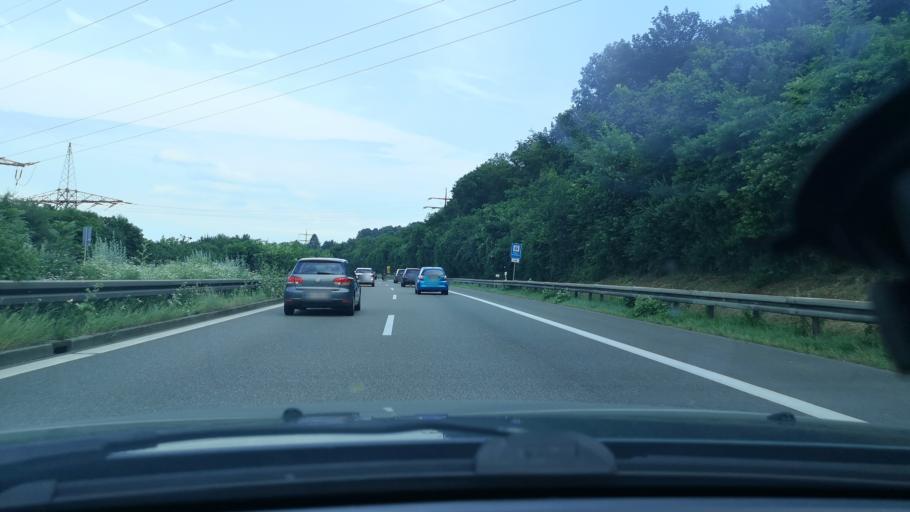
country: DE
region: Baden-Wuerttemberg
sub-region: Regierungsbezirk Stuttgart
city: Goeppingen
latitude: 48.6940
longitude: 9.6585
